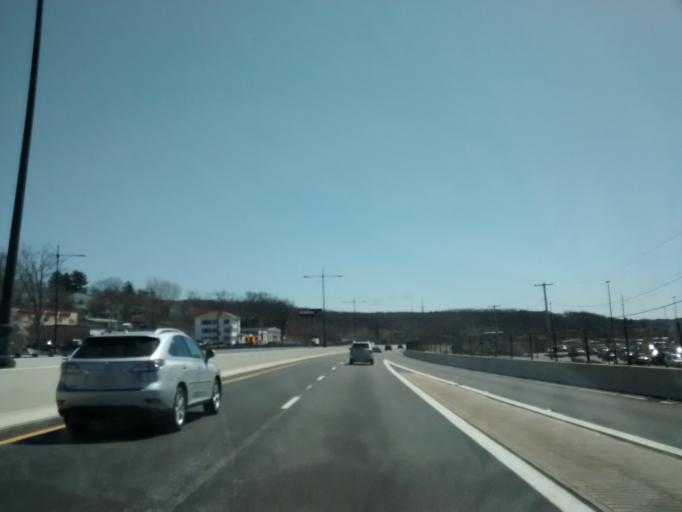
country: US
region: Massachusetts
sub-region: Worcester County
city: Sunderland
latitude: 42.2347
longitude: -71.7912
